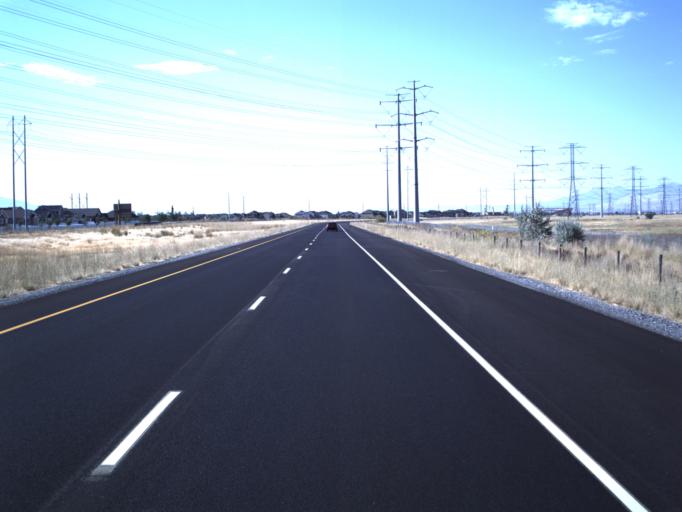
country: US
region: Utah
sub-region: Davis County
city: West Bountiful
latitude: 40.8756
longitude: -111.9381
